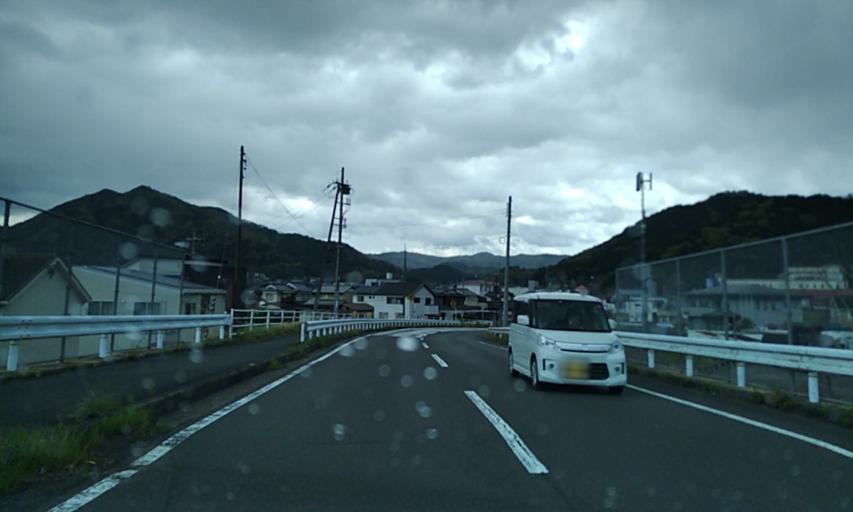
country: JP
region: Kyoto
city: Ayabe
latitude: 35.3061
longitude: 135.2314
